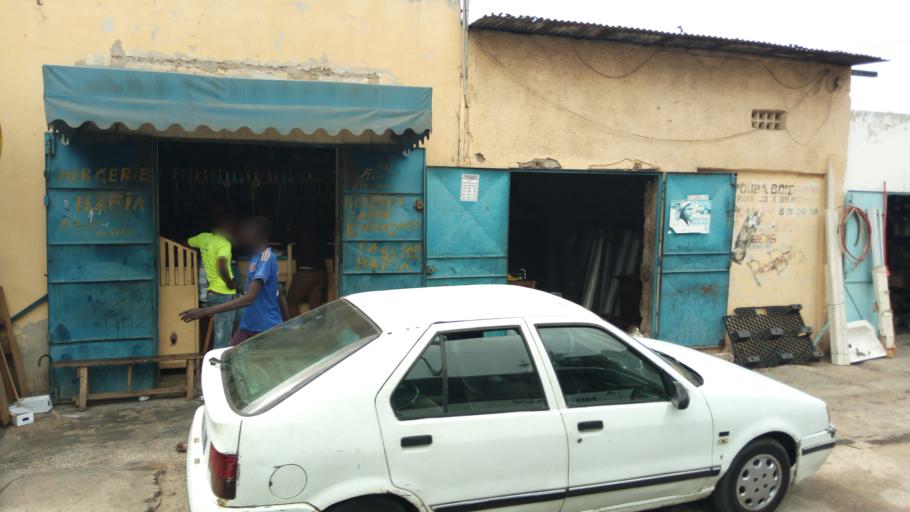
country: SN
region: Dakar
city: Dakar
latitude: 14.6863
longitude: -17.4504
